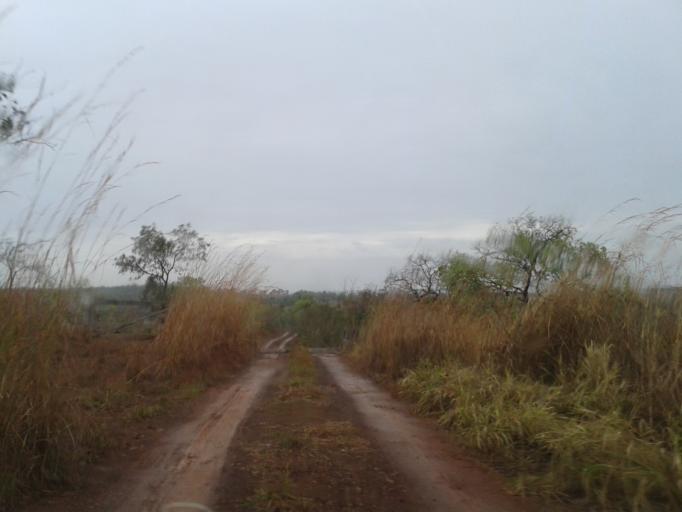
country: BR
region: Minas Gerais
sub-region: Campina Verde
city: Campina Verde
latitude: -19.3214
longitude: -49.5123
